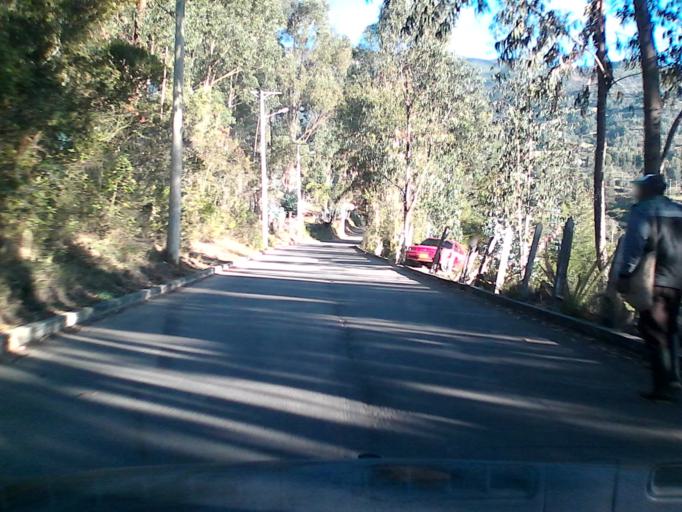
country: CO
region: Boyaca
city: Duitama
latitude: 5.8618
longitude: -73.0269
